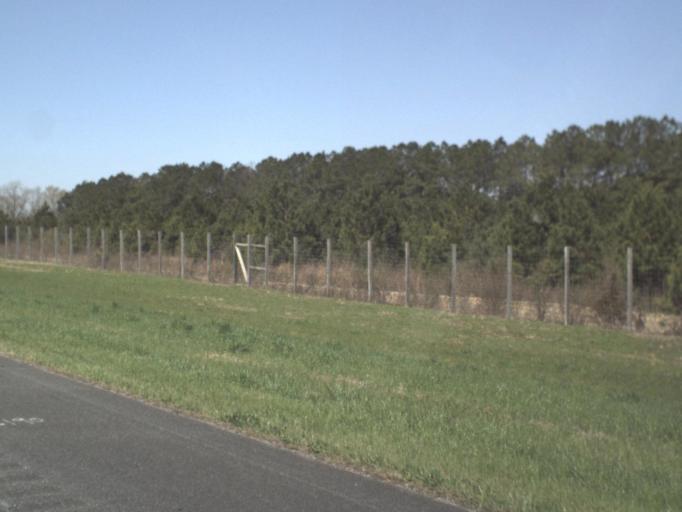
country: US
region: Florida
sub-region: Washington County
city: Chipley
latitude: 30.7502
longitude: -85.3994
